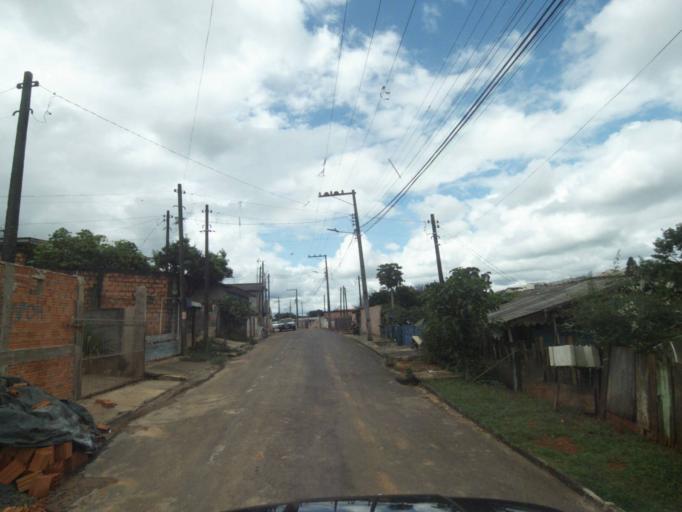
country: BR
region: Parana
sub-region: Telemaco Borba
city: Telemaco Borba
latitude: -24.3180
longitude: -50.6465
